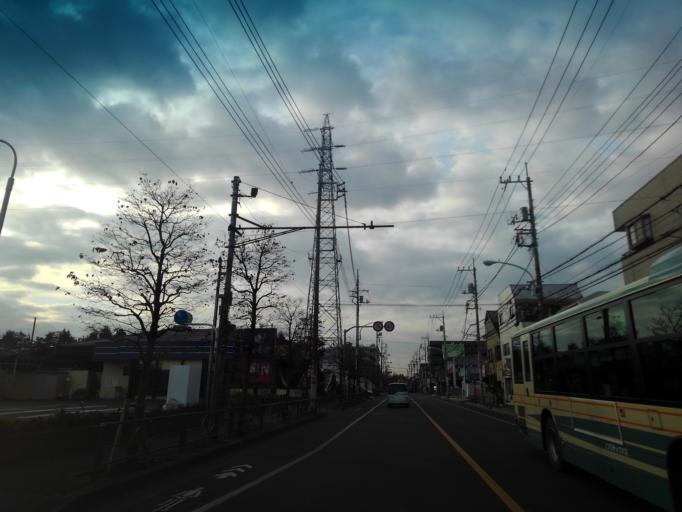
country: JP
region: Tokyo
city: Tanashicho
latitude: 35.7217
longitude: 139.5097
